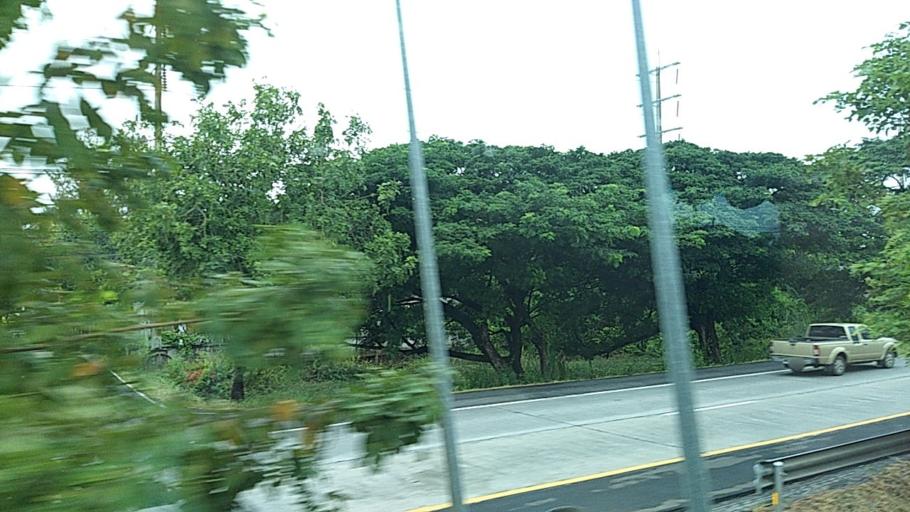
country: TH
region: Nakhon Ratchasima
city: Phimai
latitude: 15.2821
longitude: 102.4183
